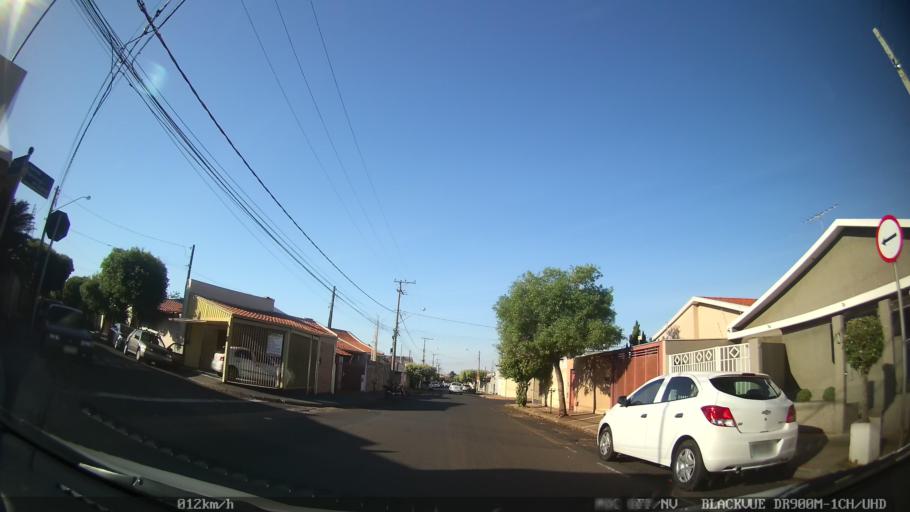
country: BR
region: Sao Paulo
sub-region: Sao Jose Do Rio Preto
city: Sao Jose do Rio Preto
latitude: -20.8117
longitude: -49.3972
